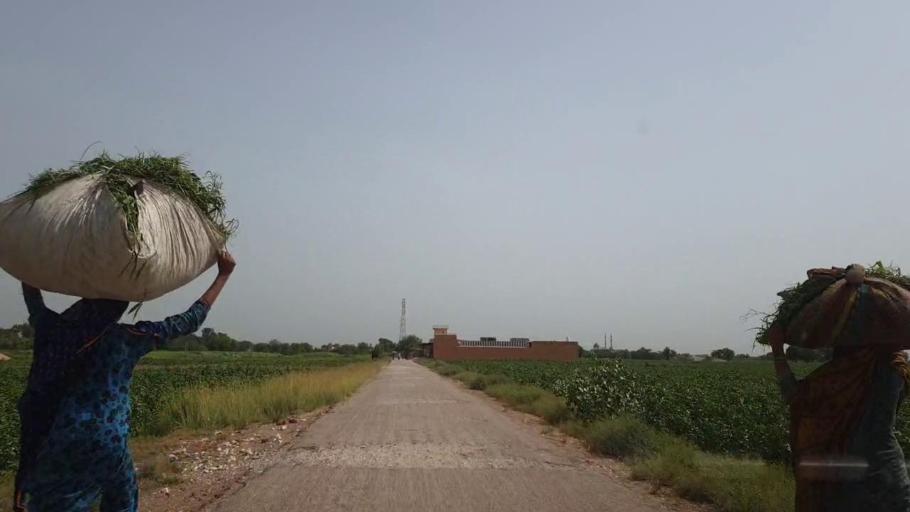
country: PK
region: Sindh
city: Sakrand
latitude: 26.1107
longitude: 68.3967
